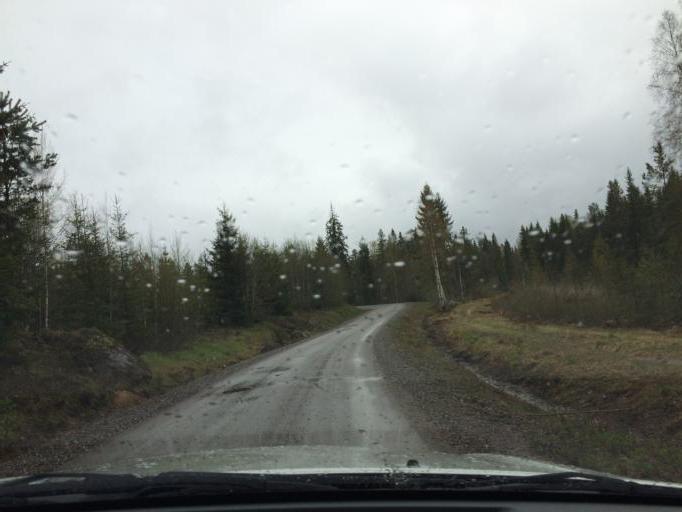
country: SE
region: OErebro
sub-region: Hallefors Kommun
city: Haellefors
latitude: 60.0196
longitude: 14.5841
